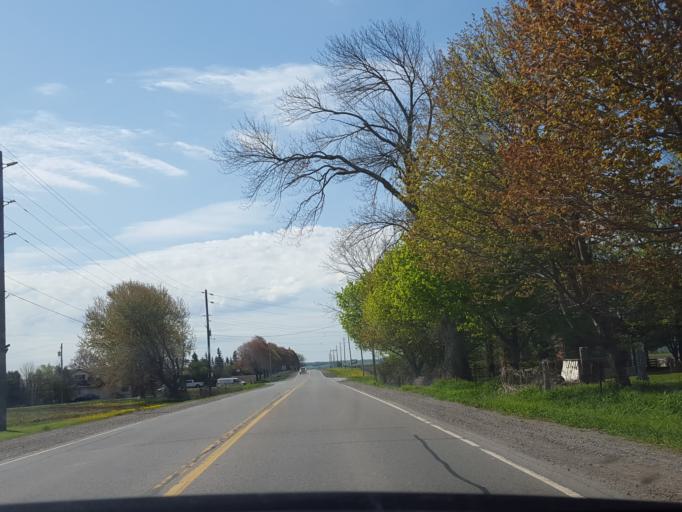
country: CA
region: Ontario
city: Uxbridge
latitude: 44.1134
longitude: -78.9202
